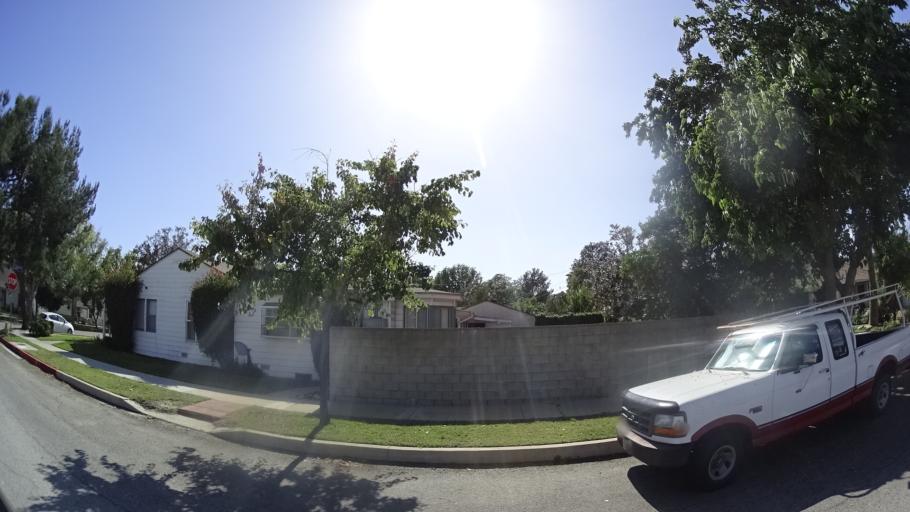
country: US
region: California
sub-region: Los Angeles County
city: North Hollywood
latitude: 34.1703
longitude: -118.3583
